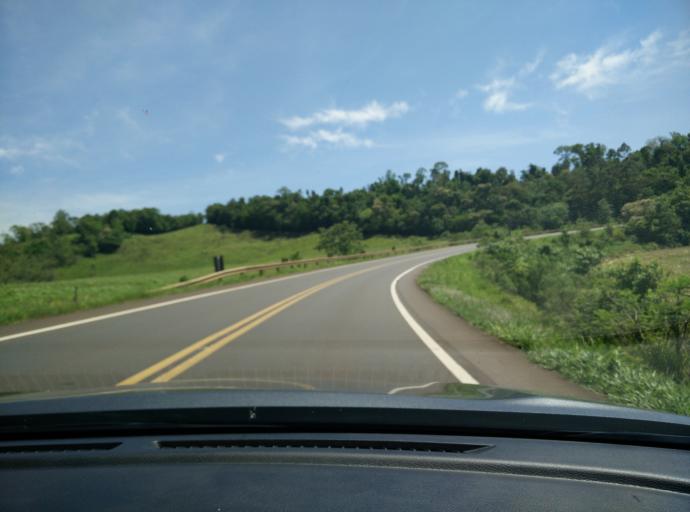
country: BR
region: Parana
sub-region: Santo Antonio Do Sudoeste
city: Santo Antonio do Sudoeste
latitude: -25.8468
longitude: -53.7542
